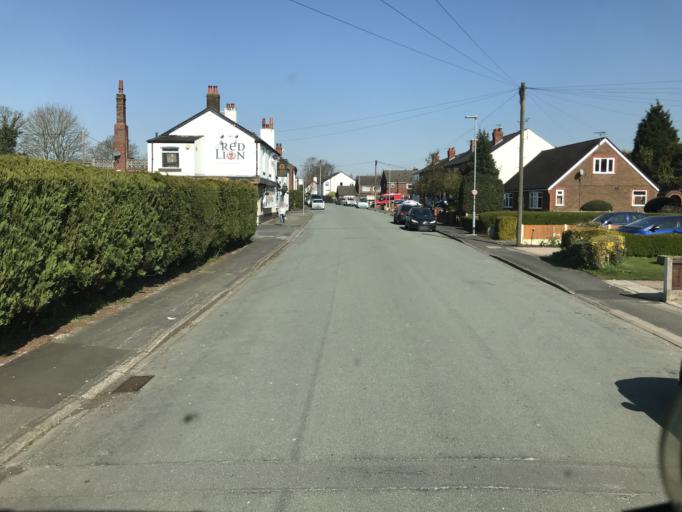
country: GB
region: England
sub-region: Trafford
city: Partington
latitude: 53.4138
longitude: -2.4564
